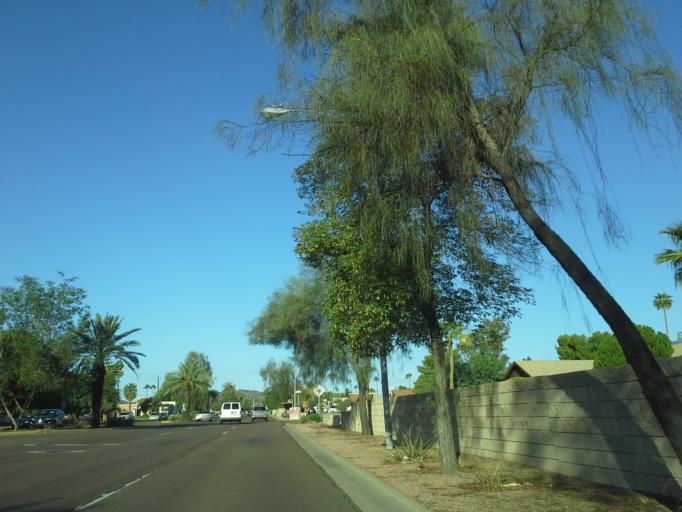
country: US
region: Arizona
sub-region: Maricopa County
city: Paradise Valley
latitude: 33.5970
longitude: -112.0236
